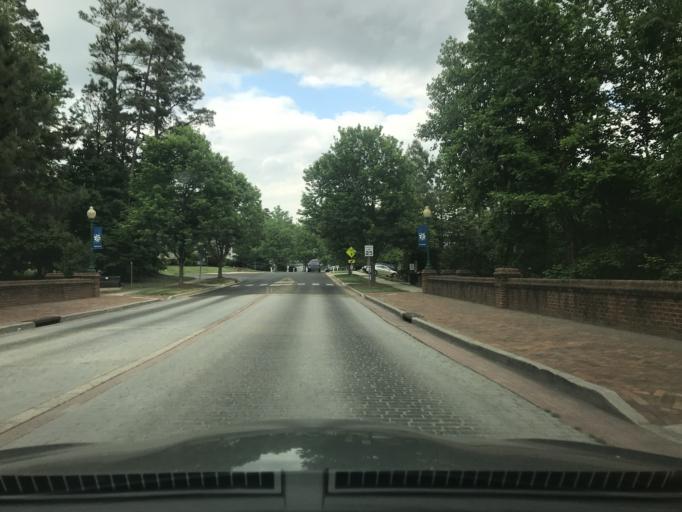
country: US
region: North Carolina
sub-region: Wake County
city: Wake Forest
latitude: 35.9122
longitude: -78.5864
